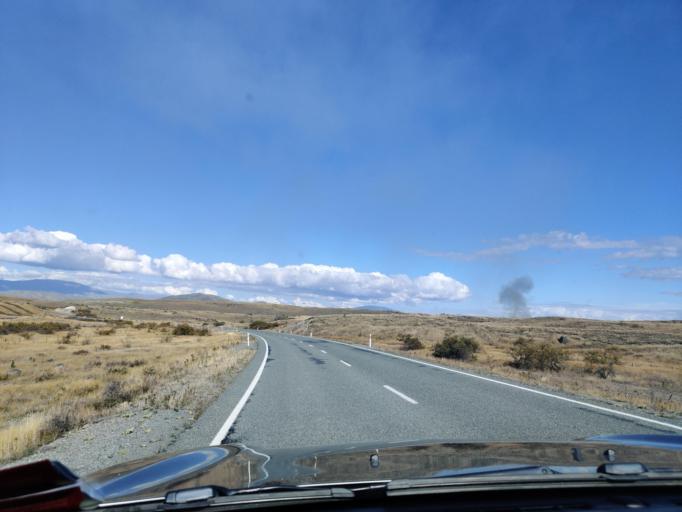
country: NZ
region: Canterbury
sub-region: Timaru District
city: Pleasant Point
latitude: -44.1758
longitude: 170.2172
